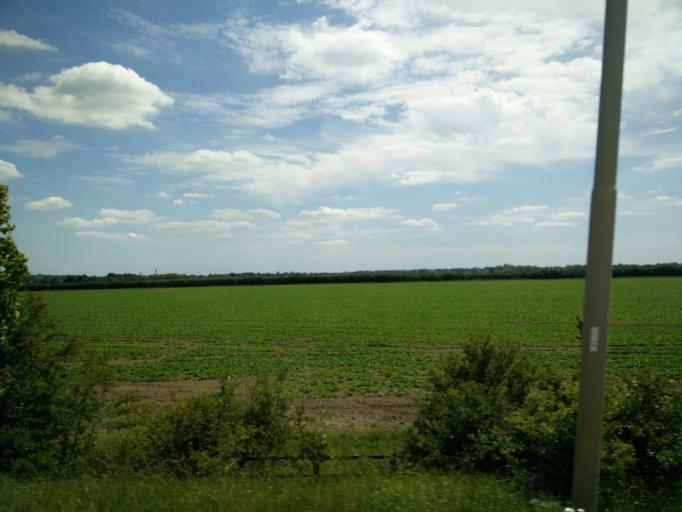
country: GB
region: England
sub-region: Cambridgeshire
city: Grantchester
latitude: 52.1613
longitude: 0.1052
